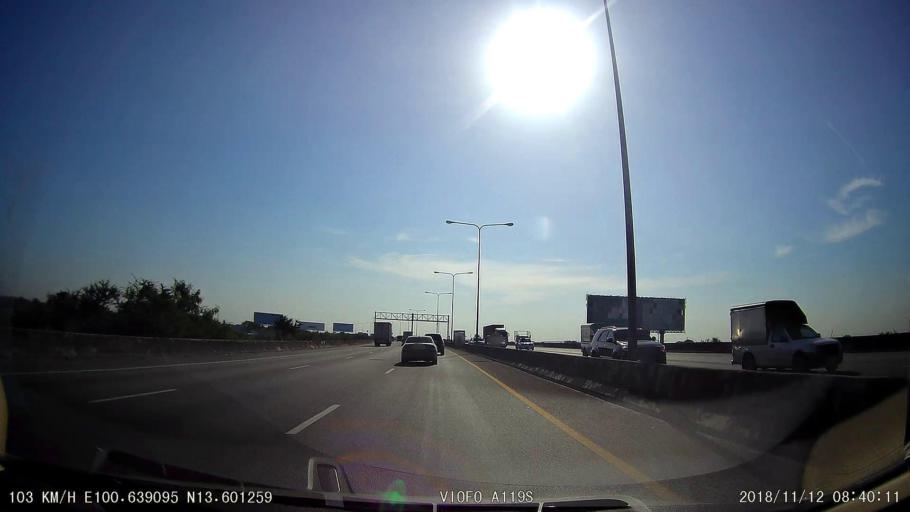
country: TH
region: Samut Prakan
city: Samut Prakan
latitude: 13.6008
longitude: 100.6402
